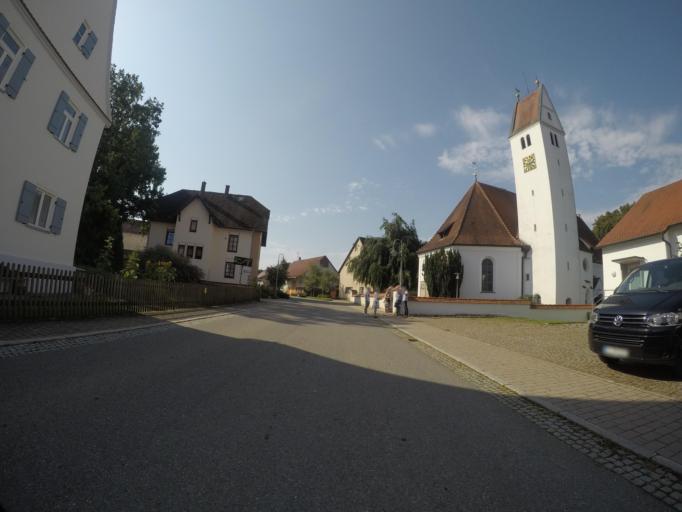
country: DE
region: Baden-Wuerttemberg
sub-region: Tuebingen Region
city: Wain
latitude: 48.1899
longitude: 10.0200
